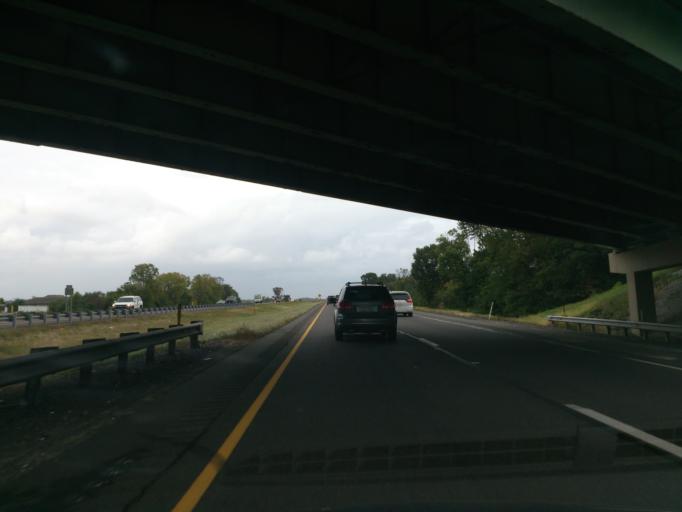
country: US
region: Pennsylvania
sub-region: Lancaster County
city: Brownstown
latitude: 40.1247
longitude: -76.2203
